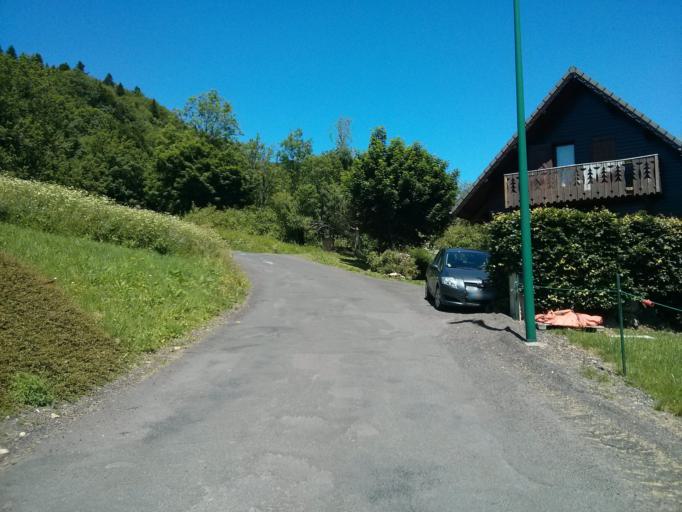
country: FR
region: Auvergne
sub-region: Departement du Puy-de-Dome
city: Mont-Dore
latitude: 45.5893
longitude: 2.8002
